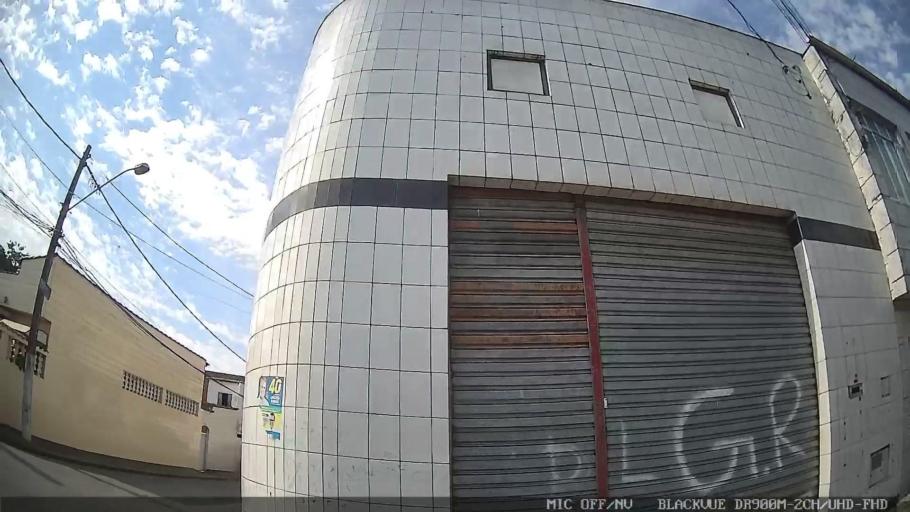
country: BR
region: Sao Paulo
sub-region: Santos
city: Santos
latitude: -23.9495
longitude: -46.2934
